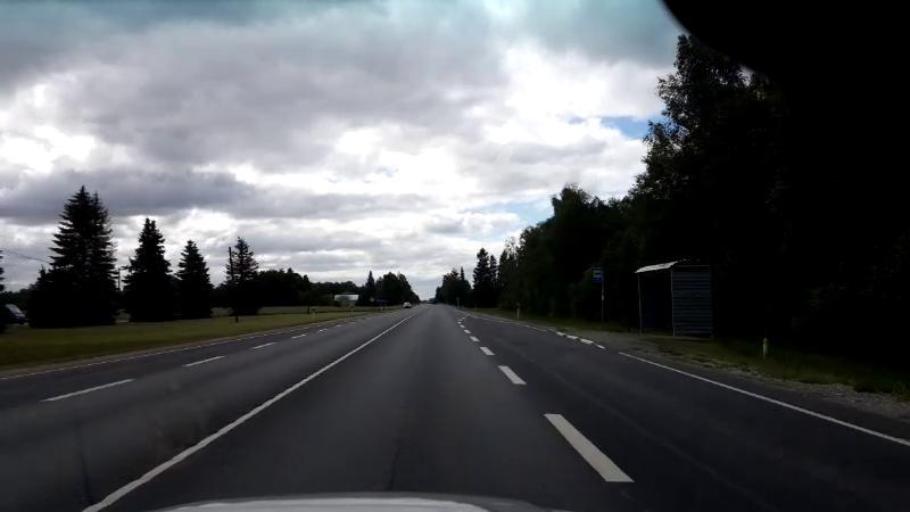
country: EE
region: Paernumaa
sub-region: Halinga vald
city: Parnu-Jaagupi
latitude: 58.6549
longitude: 24.4756
